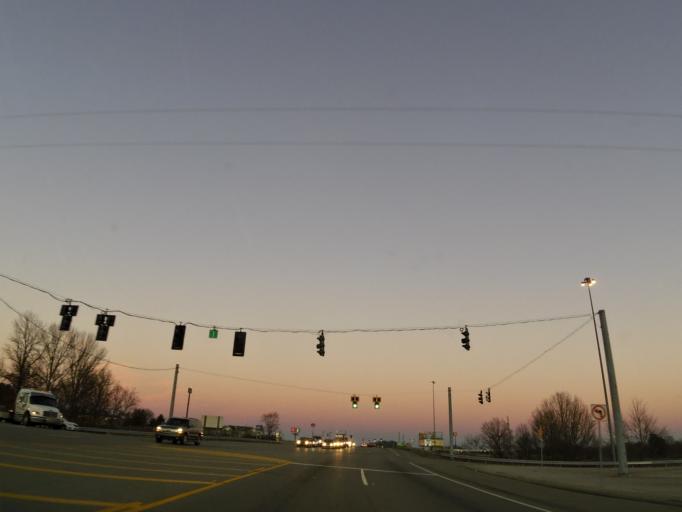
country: US
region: Kentucky
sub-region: Laurel County
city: London
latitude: 37.1098
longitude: -84.1040
